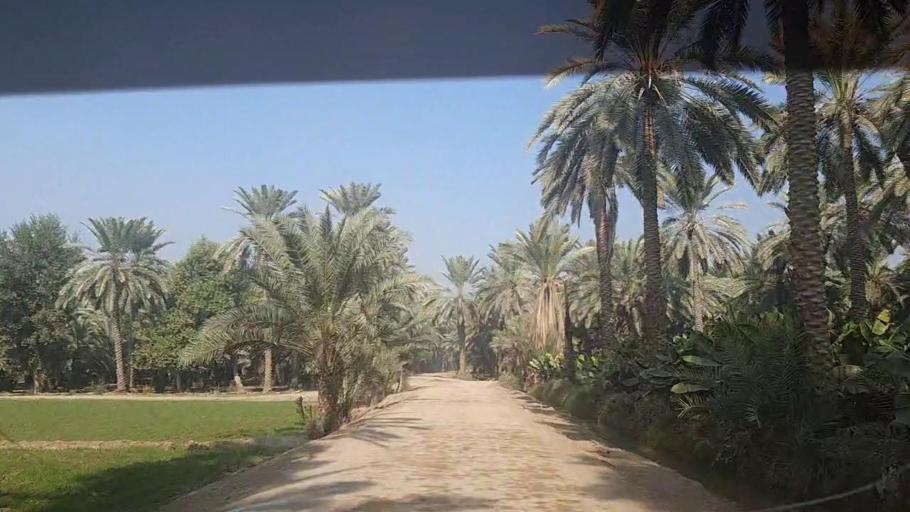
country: PK
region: Sindh
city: Khairpur
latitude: 27.4630
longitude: 68.7178
